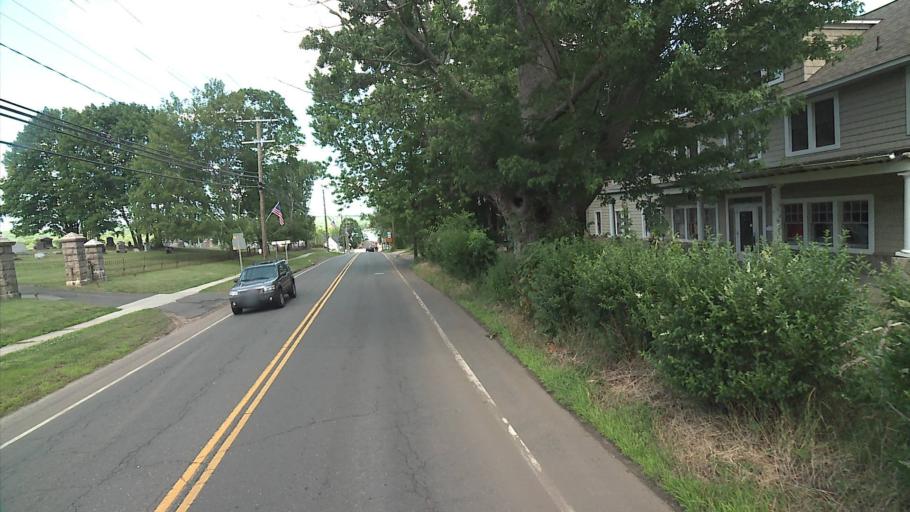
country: US
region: Connecticut
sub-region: Middlesex County
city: East Hampton
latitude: 41.5829
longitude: -72.4974
